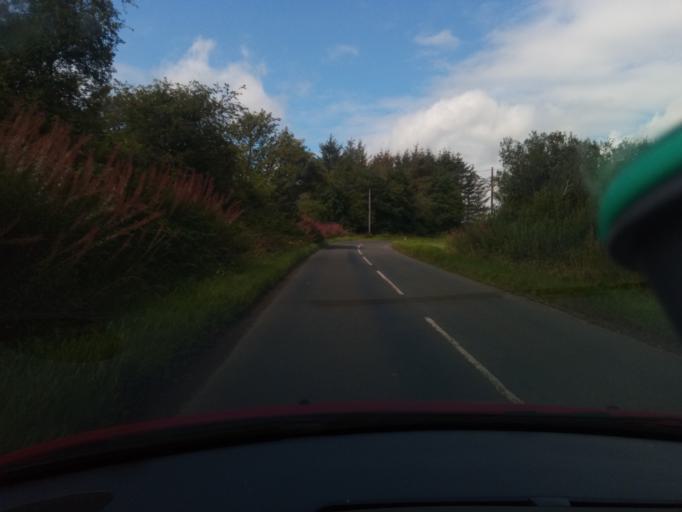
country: GB
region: Scotland
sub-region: The Scottish Borders
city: Melrose
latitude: 55.5702
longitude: -2.7302
